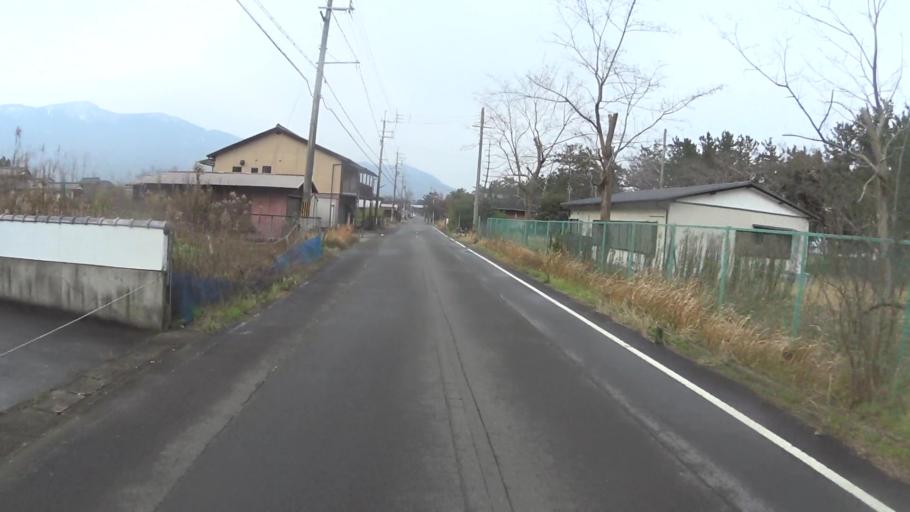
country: JP
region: Kyoto
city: Maizuru
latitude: 35.5126
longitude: 135.3033
